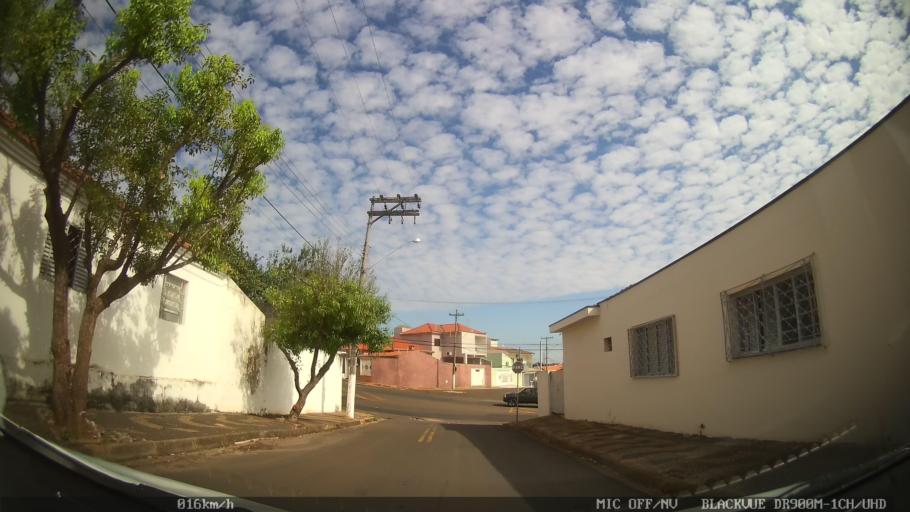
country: BR
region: Sao Paulo
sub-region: Santa Barbara D'Oeste
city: Santa Barbara d'Oeste
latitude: -22.7580
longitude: -47.4050
